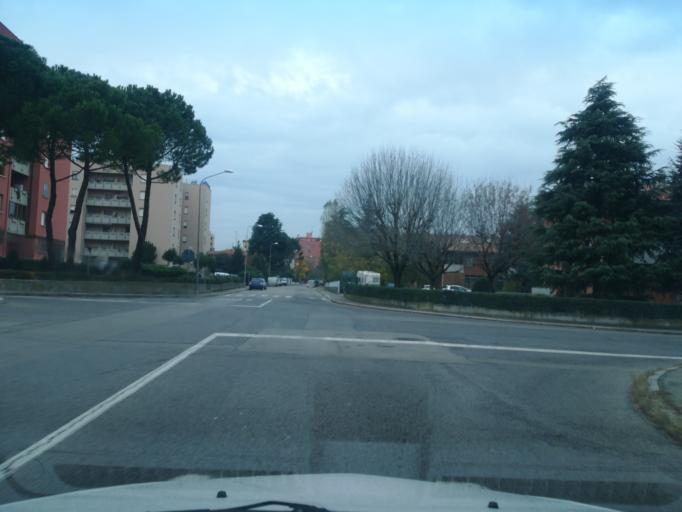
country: IT
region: Emilia-Romagna
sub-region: Provincia di Bologna
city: Imola
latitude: 44.3653
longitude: 11.6894
